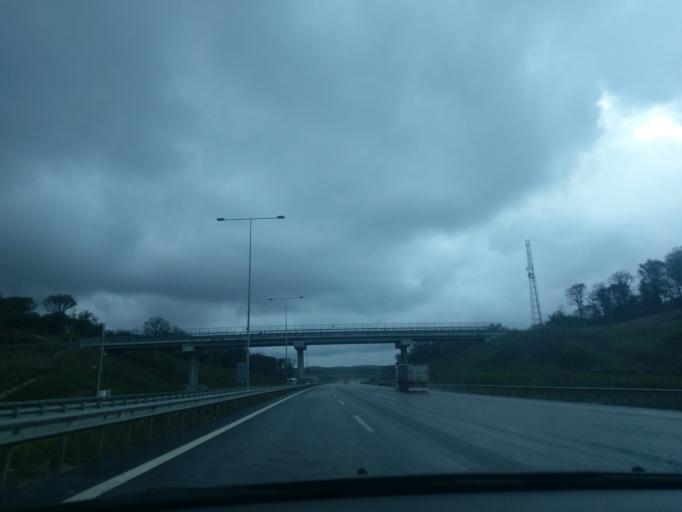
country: TR
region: Istanbul
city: Kemerburgaz
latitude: 41.2343
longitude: 28.9175
